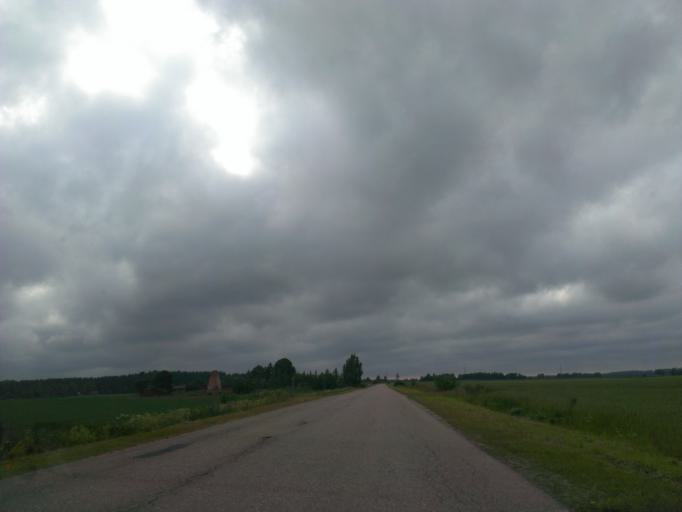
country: LV
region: Aizpute
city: Aizpute
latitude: 56.7158
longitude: 21.4614
